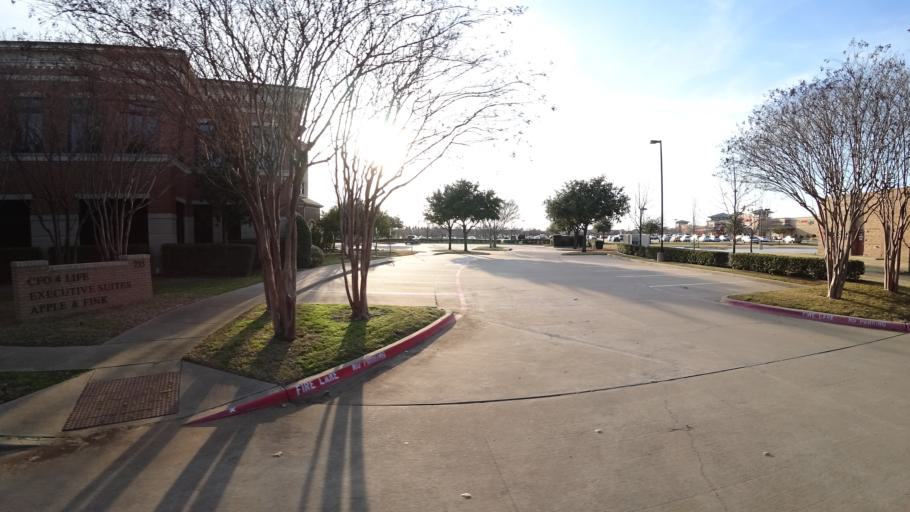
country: US
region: Texas
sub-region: Dallas County
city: Coppell
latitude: 32.9877
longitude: -96.9901
